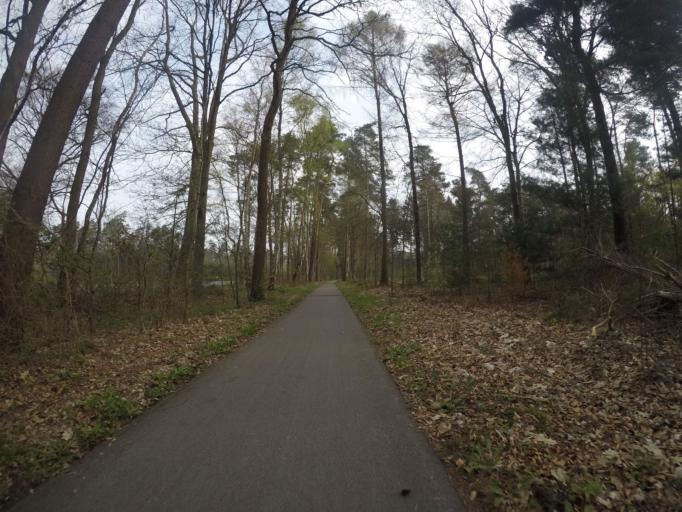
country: DE
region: North Rhine-Westphalia
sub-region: Regierungsbezirk Munster
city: Isselburg
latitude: 51.8382
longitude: 6.4974
